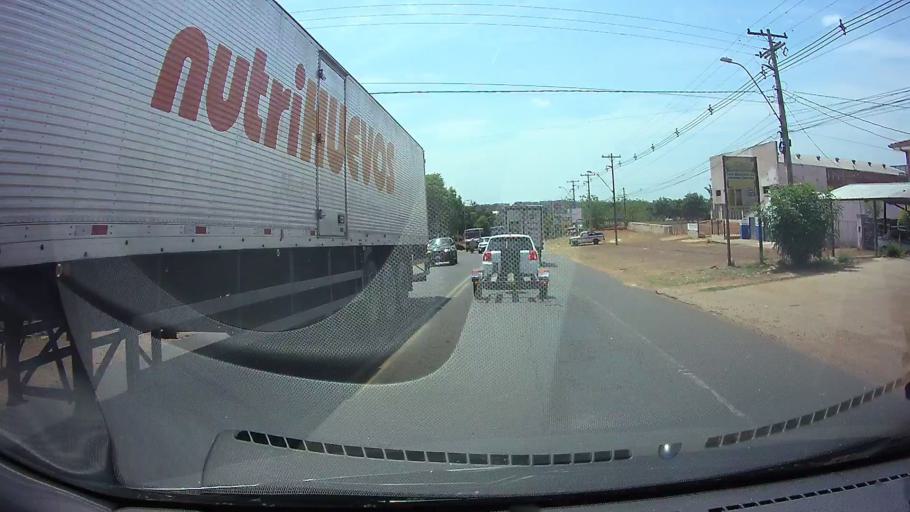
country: PY
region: Central
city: Capiata
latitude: -25.3974
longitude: -57.4661
